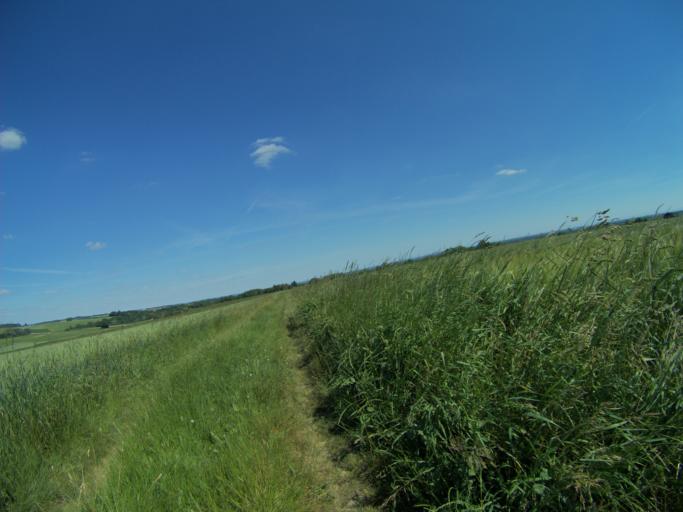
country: DE
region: Bavaria
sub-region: Upper Bavaria
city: Marzling
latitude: 48.4136
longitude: 11.7716
